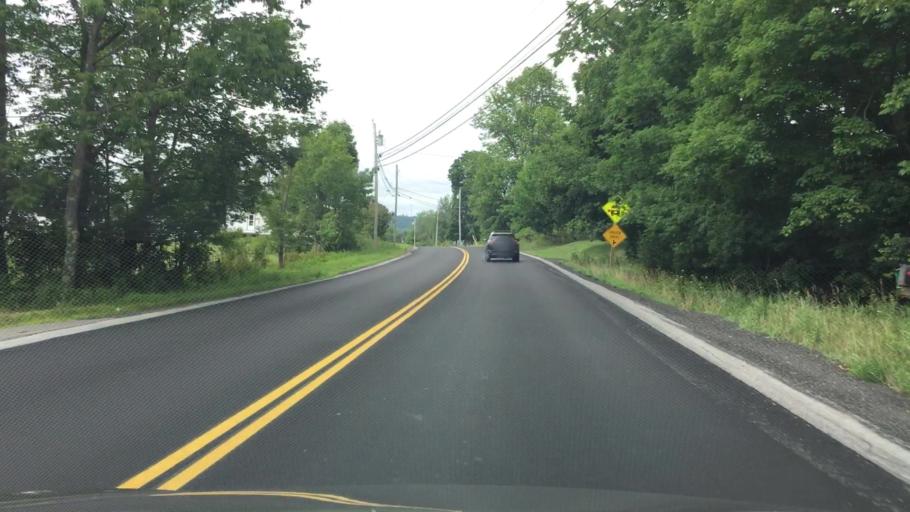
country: US
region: Maine
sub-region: Waldo County
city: Winterport
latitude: 44.6268
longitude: -68.8331
